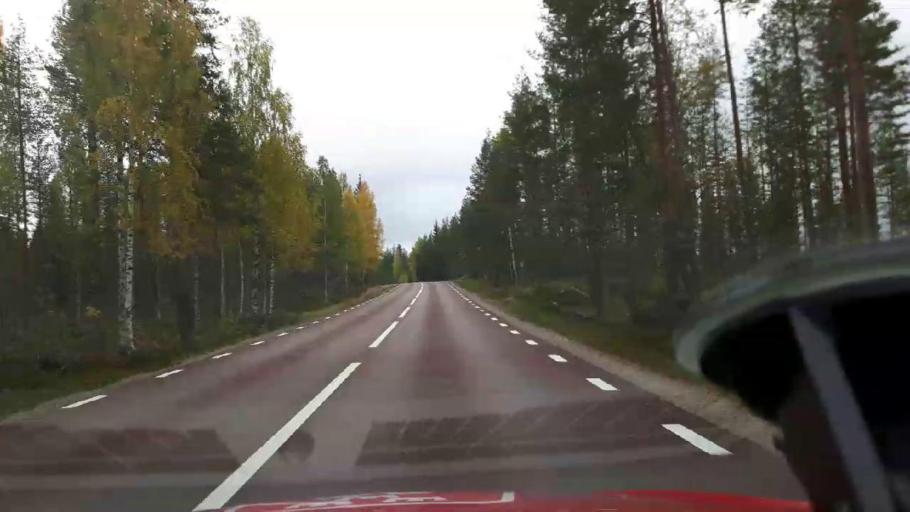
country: SE
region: Jaemtland
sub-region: Harjedalens Kommun
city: Sveg
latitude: 62.2114
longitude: 14.8444
